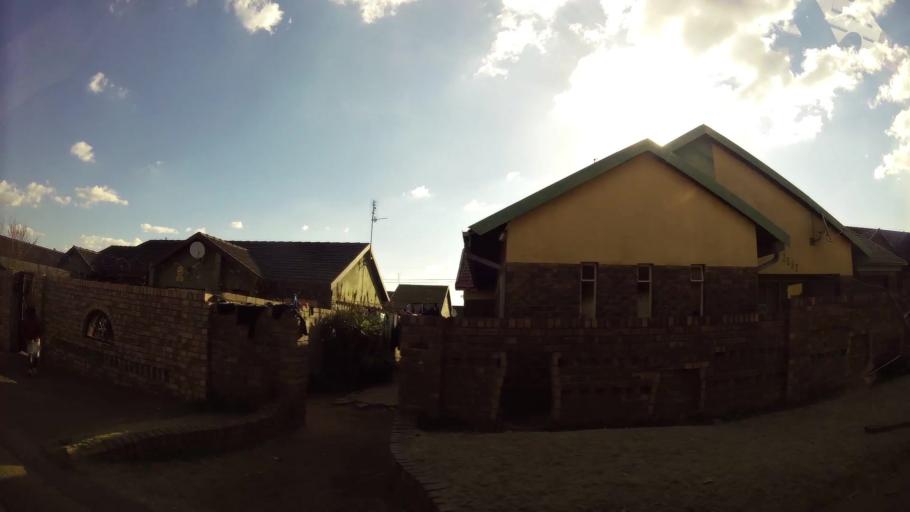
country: ZA
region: Mpumalanga
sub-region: Nkangala District Municipality
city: Witbank
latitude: -25.8718
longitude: 29.1844
